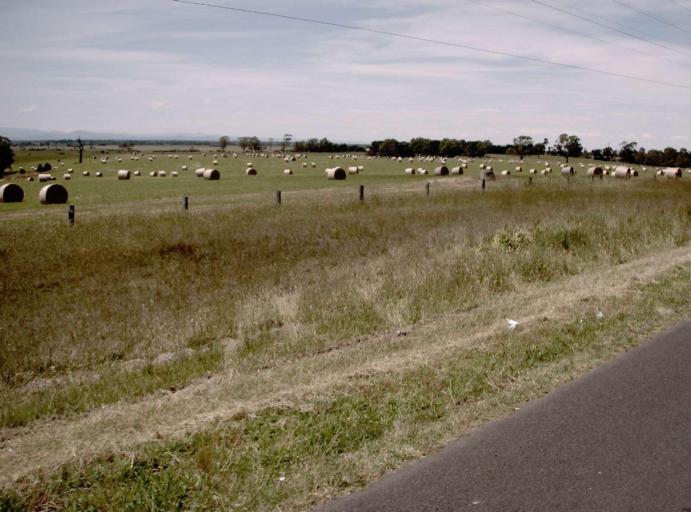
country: AU
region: Victoria
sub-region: Latrobe
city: Traralgon
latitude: -38.1806
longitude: 146.6205
